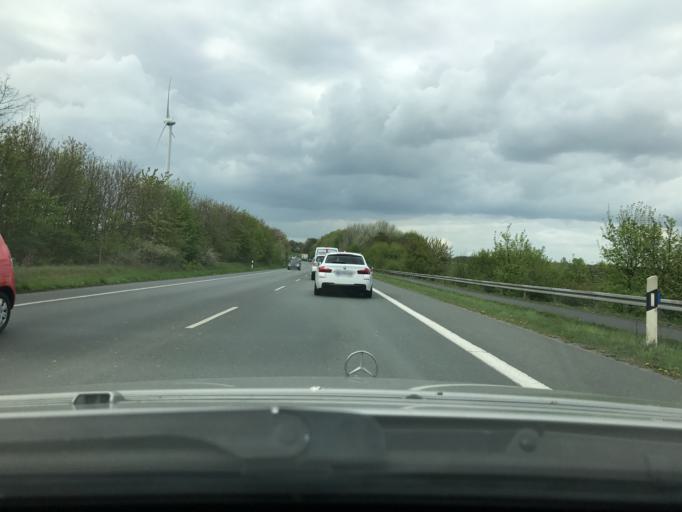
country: DE
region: North Rhine-Westphalia
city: Waltrop
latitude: 51.5936
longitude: 7.3929
